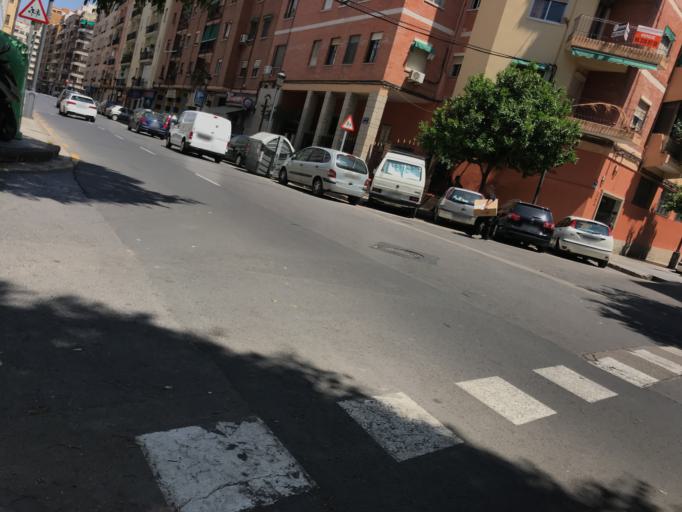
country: ES
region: Valencia
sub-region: Provincia de Valencia
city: Valencia
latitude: 39.4652
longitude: -0.3932
